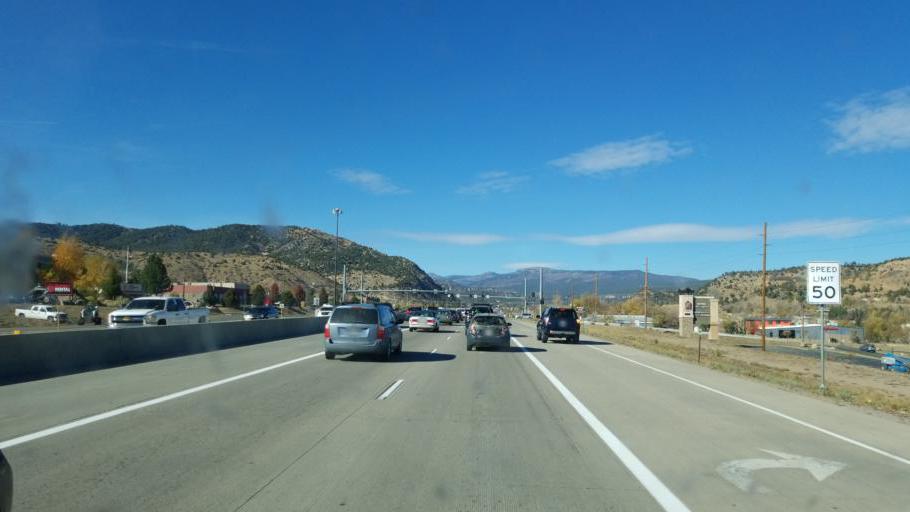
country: US
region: Colorado
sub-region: La Plata County
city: Durango
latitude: 37.2405
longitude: -107.8713
